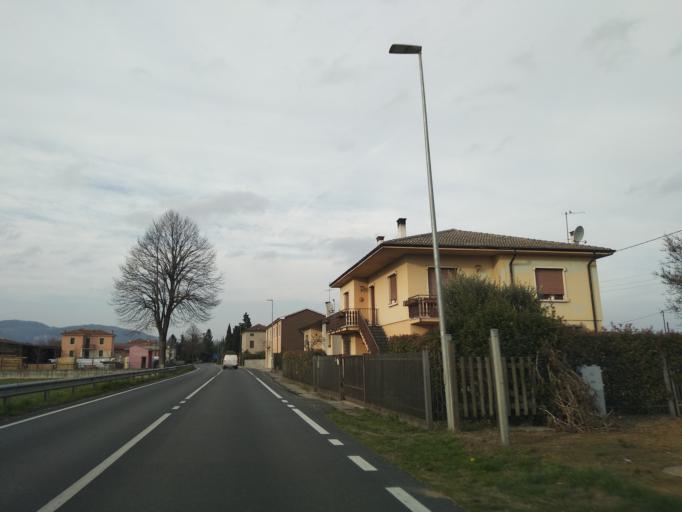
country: IT
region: Veneto
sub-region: Provincia di Vicenza
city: Ponte di Castegnero
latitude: 45.4334
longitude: 11.5986
